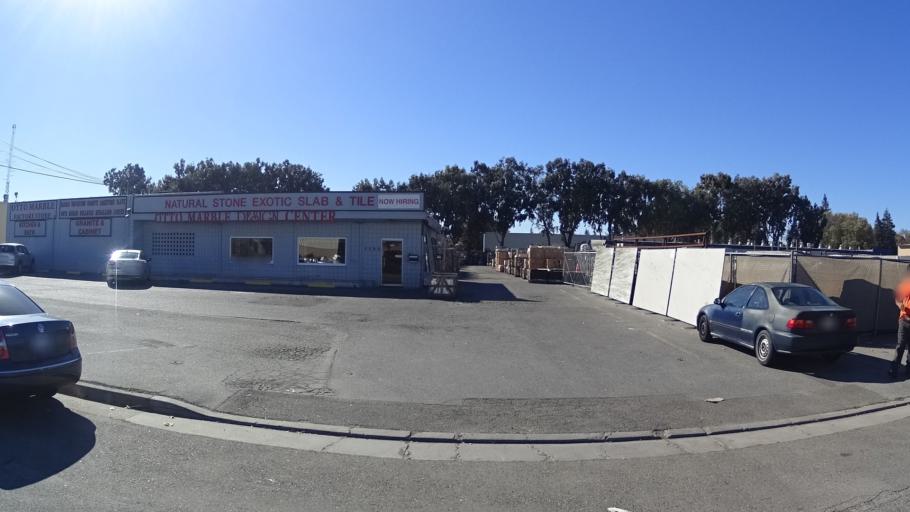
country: US
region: California
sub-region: Santa Clara County
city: San Jose
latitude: 37.3779
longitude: -121.9103
